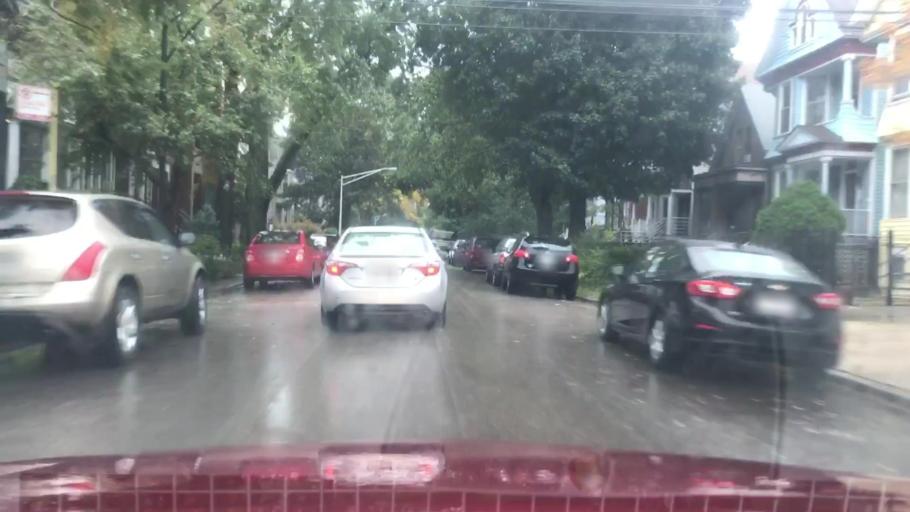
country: US
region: Illinois
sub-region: Cook County
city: Chicago
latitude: 41.9361
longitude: -87.6681
